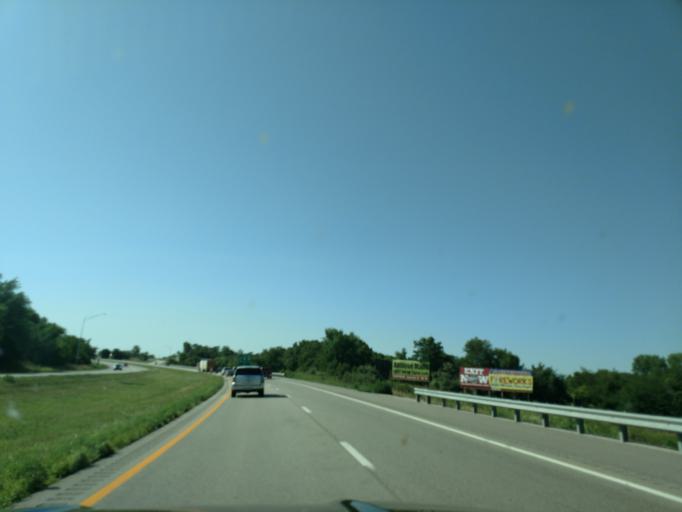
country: US
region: Missouri
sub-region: Andrew County
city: Country Club Village
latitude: 39.8534
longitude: -94.8052
